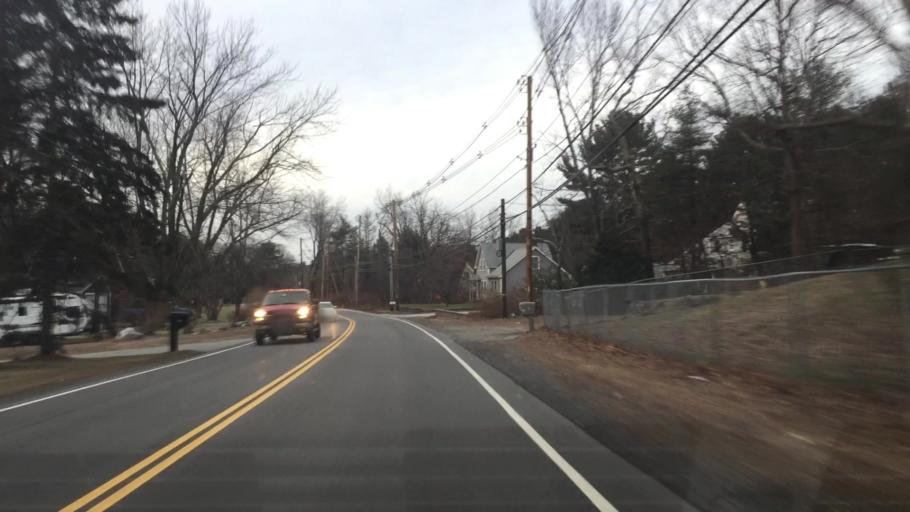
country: US
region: New Hampshire
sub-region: Hillsborough County
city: Pelham
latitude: 42.7440
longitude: -71.2903
